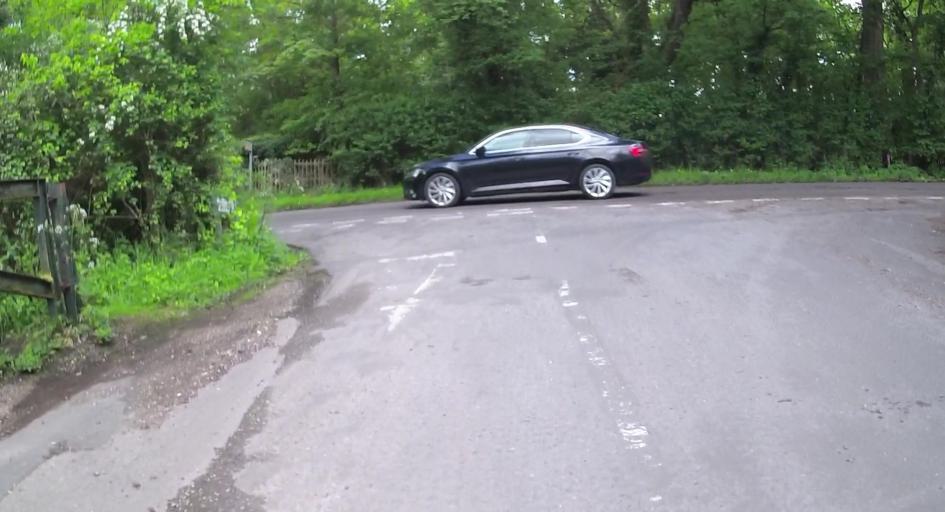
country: GB
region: England
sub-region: Wokingham
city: Swallowfield
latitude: 51.3605
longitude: -0.9859
